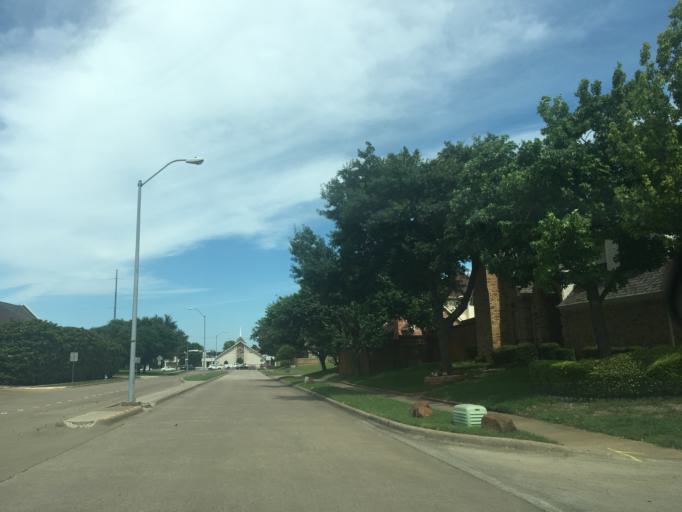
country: US
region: Texas
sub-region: Dallas County
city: Richardson
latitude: 32.9384
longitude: -96.6851
